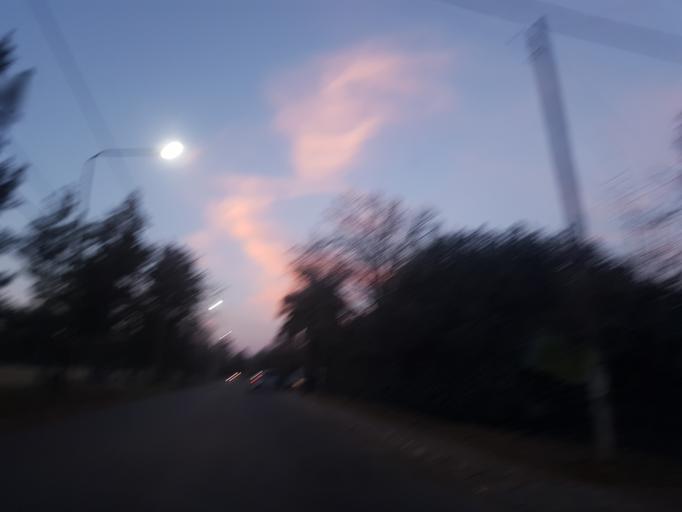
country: AR
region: Cordoba
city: Villa Allende
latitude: -31.2823
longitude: -64.2879
